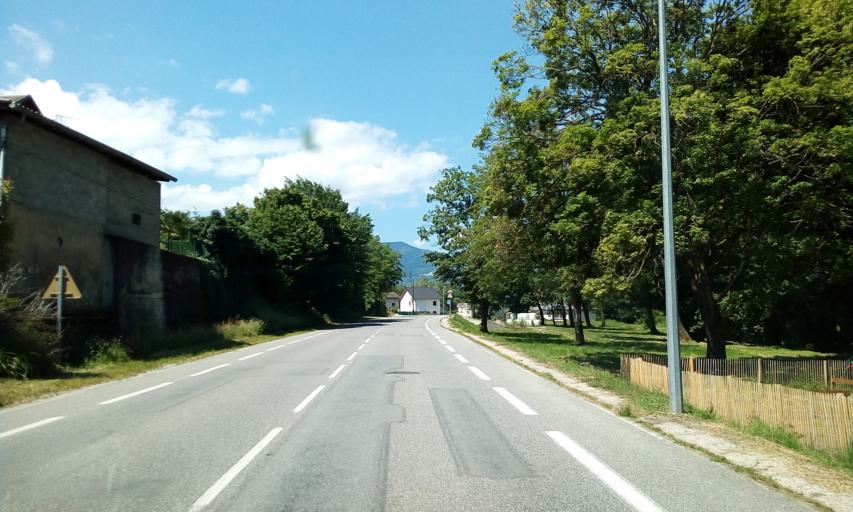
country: FR
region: Rhone-Alpes
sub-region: Departement de la Savoie
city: Montmelian
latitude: 45.5018
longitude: 6.0318
